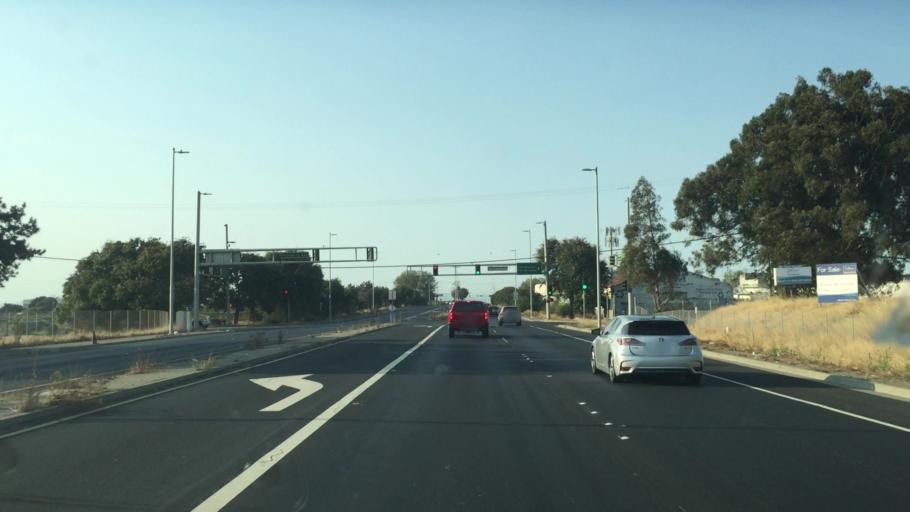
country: US
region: California
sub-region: Contra Costa County
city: North Richmond
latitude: 37.9624
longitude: -122.3737
